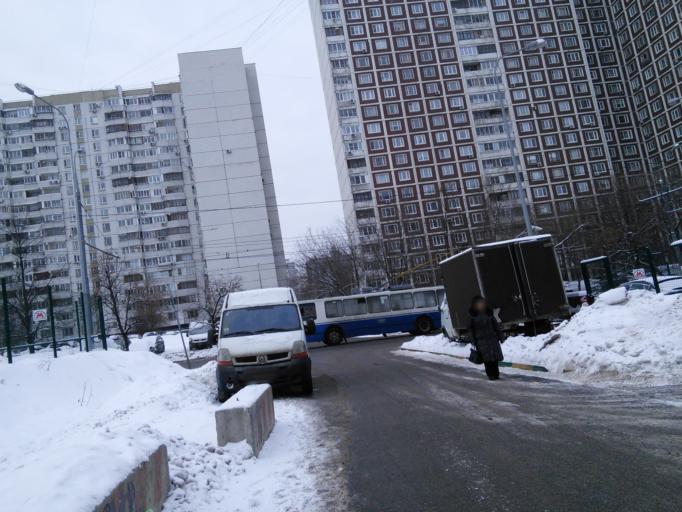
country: RU
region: Moscow
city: Orekhovo-Borisovo
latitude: 55.6206
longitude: 37.7438
